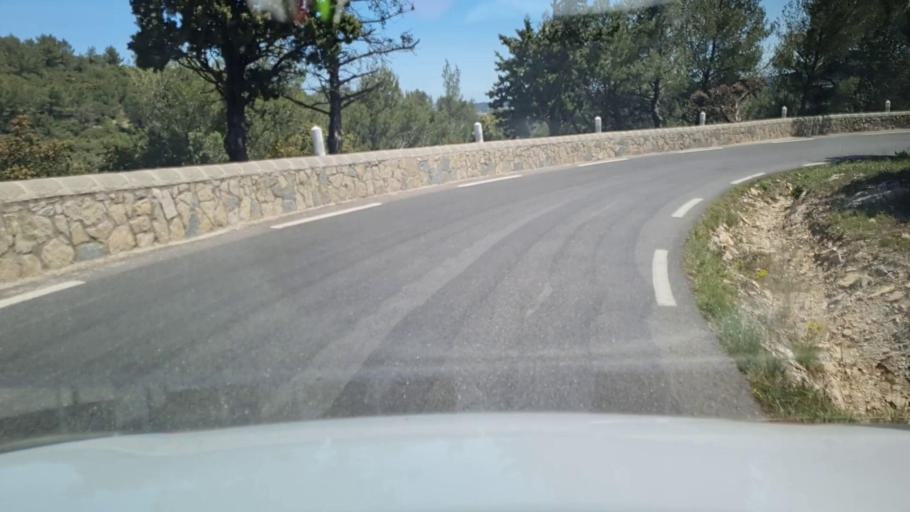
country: FR
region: Languedoc-Roussillon
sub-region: Departement du Gard
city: Clarensac
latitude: 43.8363
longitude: 4.2275
